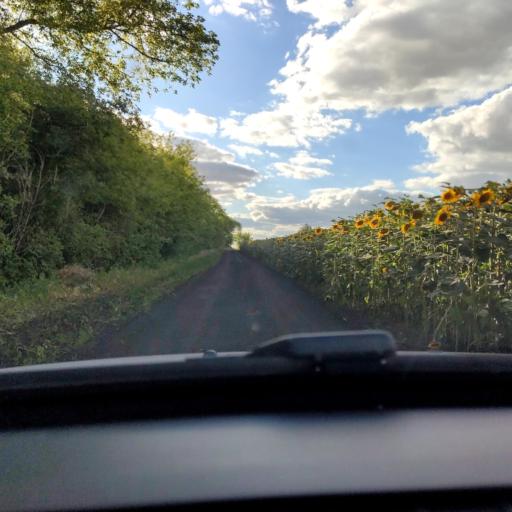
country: RU
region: Voronezj
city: Verkhnyaya Khava
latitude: 51.5931
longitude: 39.8449
